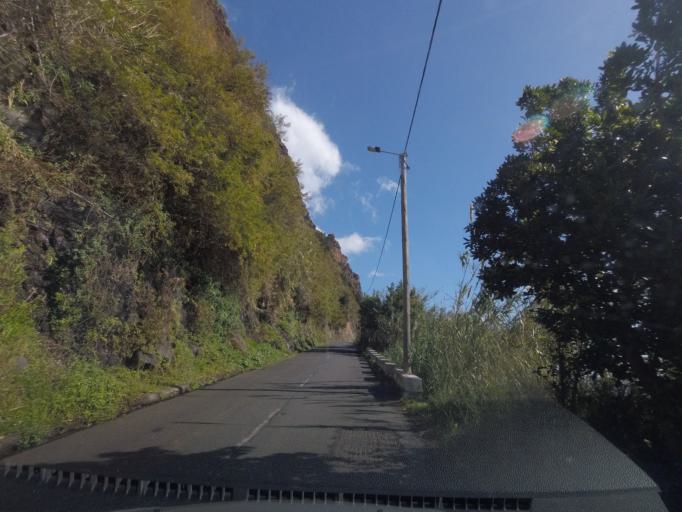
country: PT
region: Madeira
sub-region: Calheta
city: Estreito da Calheta
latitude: 32.7344
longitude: -17.2058
